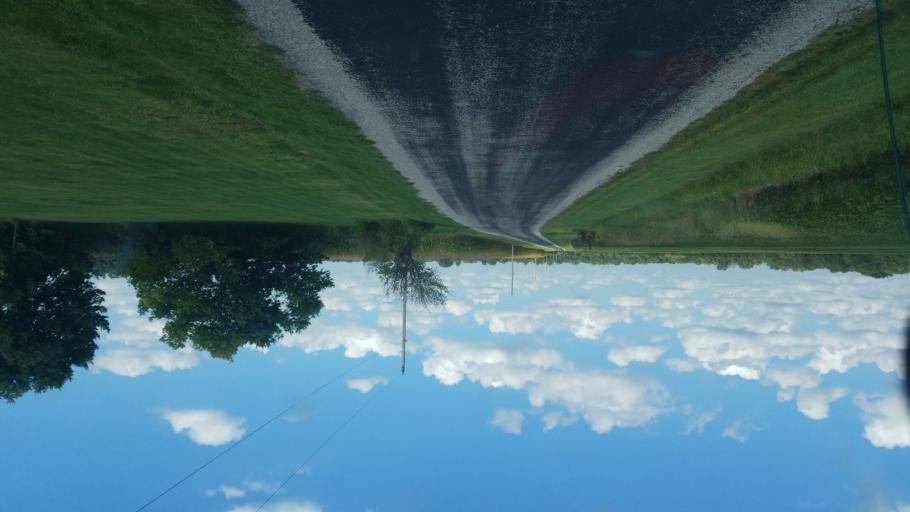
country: US
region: Ohio
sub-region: Marion County
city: Prospect
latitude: 40.3604
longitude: -83.1999
